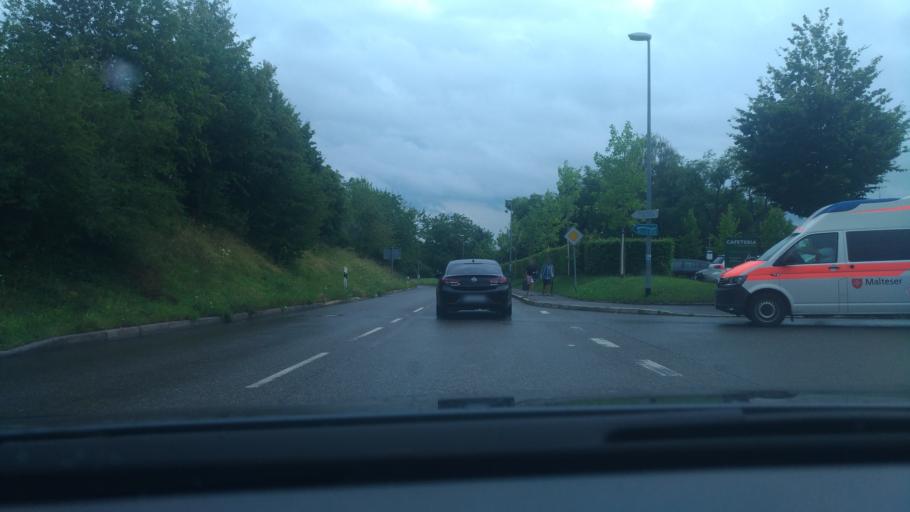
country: DE
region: Baden-Wuerttemberg
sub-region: Tuebingen Region
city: Uberlingen
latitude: 47.7756
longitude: 9.1521
